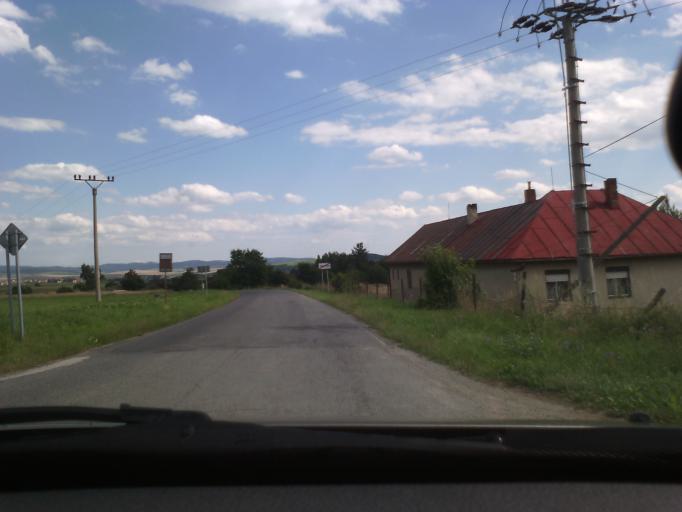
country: SK
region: Presovsky
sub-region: Okres Poprad
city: Nova Lesna
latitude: 49.1336
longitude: 20.3125
